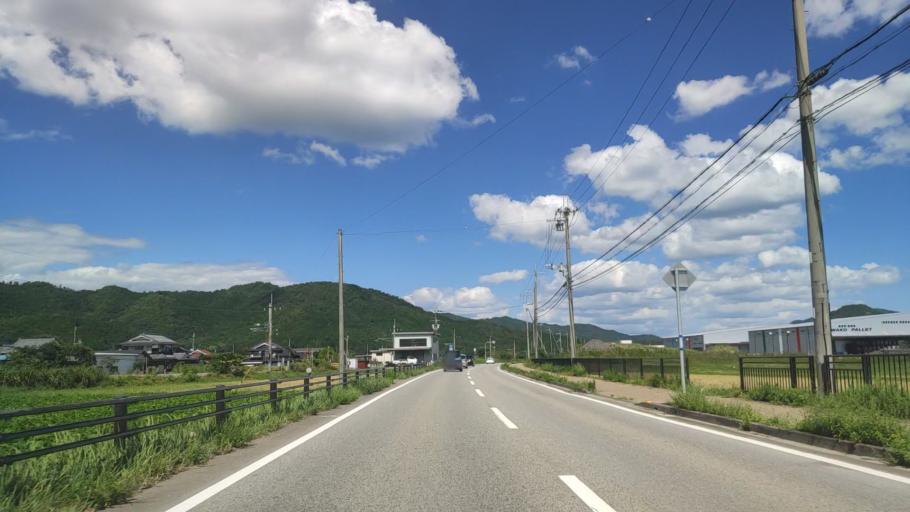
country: JP
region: Kyoto
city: Fukuchiyama
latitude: 35.1701
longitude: 135.1175
